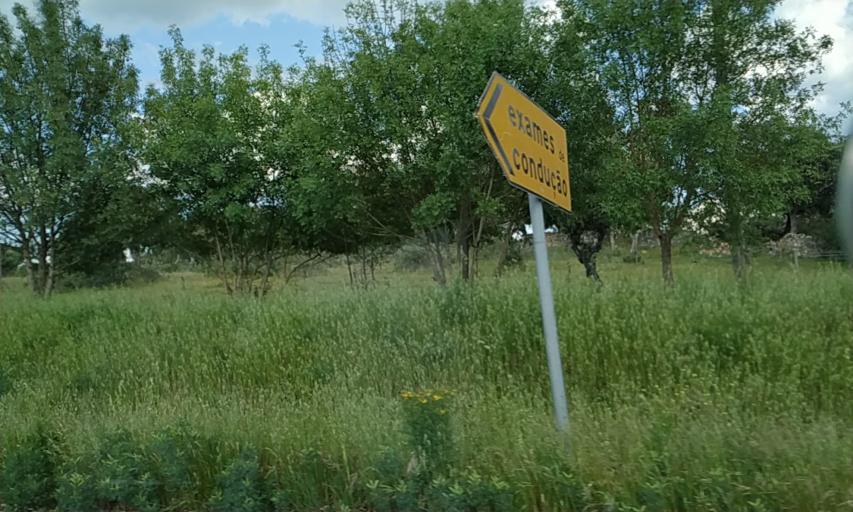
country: PT
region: Portalegre
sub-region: Portalegre
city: Portalegre
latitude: 39.2548
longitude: -7.4472
